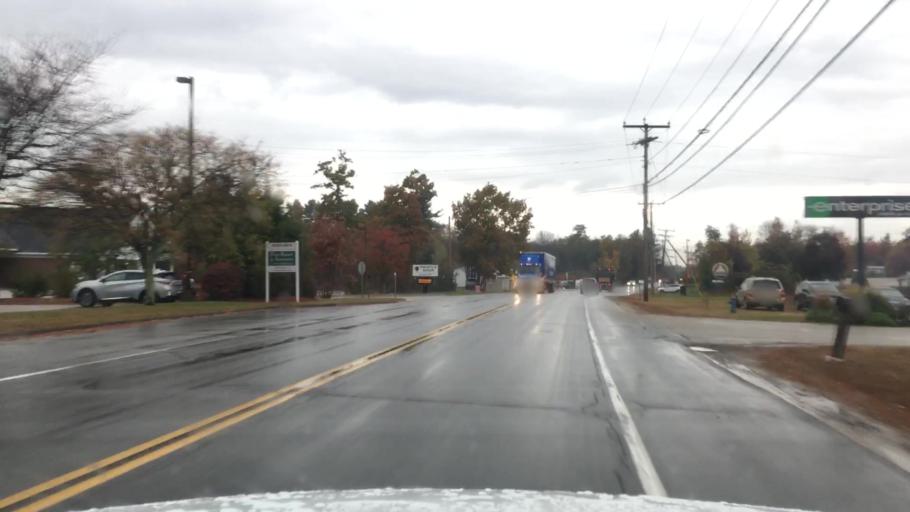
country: US
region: New Hampshire
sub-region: Strafford County
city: Somersworth
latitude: 43.2363
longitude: -70.8980
